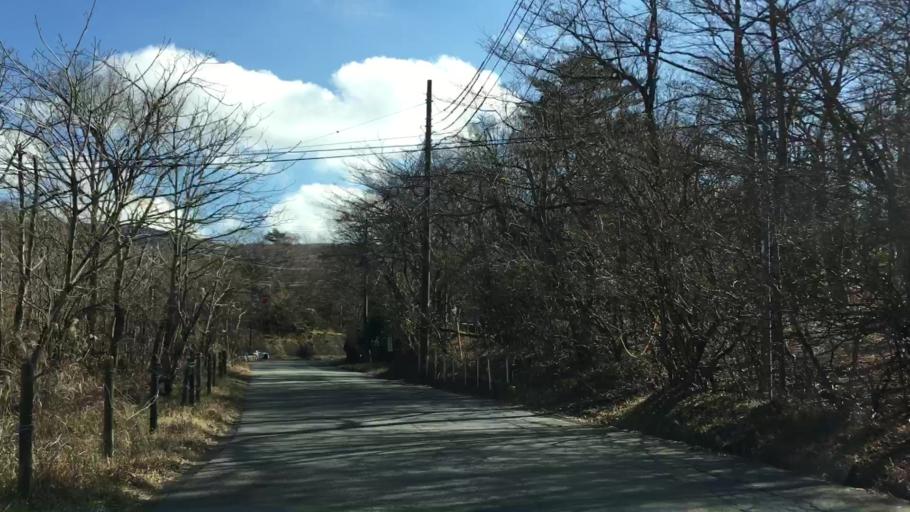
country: JP
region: Shizuoka
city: Gotemba
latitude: 35.3945
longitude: 138.8630
